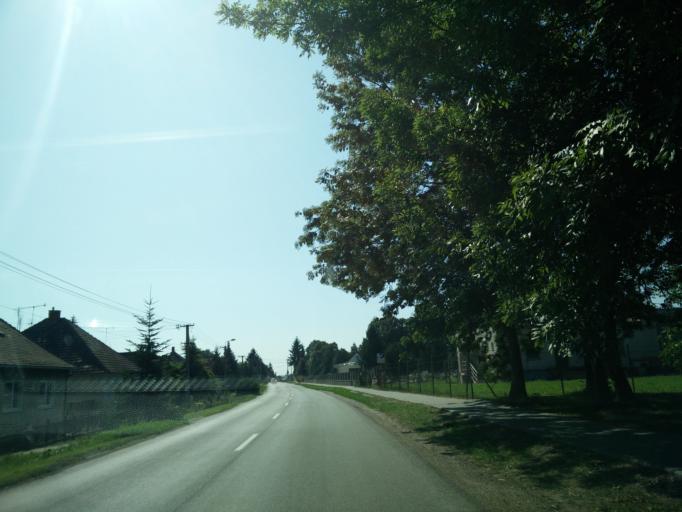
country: SK
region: Nitriansky
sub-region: Okres Nitra
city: Nitra
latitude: 48.3517
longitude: 18.0251
